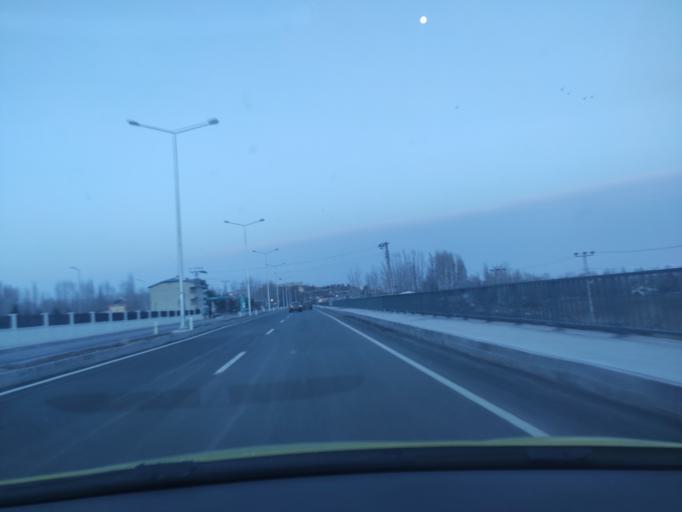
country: TR
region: Bayburt
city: Aydintepe
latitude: 40.3879
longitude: 40.1406
